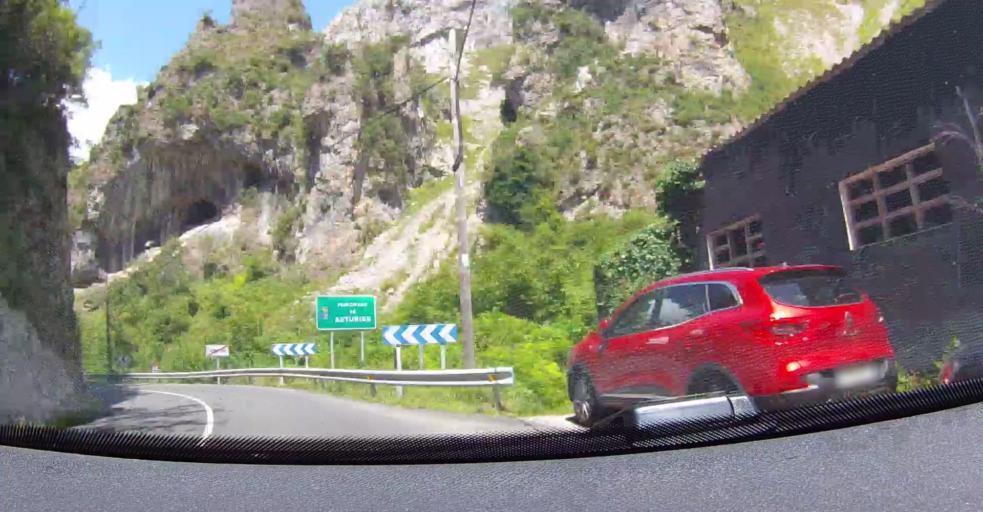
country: ES
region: Cantabria
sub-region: Provincia de Cantabria
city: Tresviso
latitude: 43.2676
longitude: -4.6318
